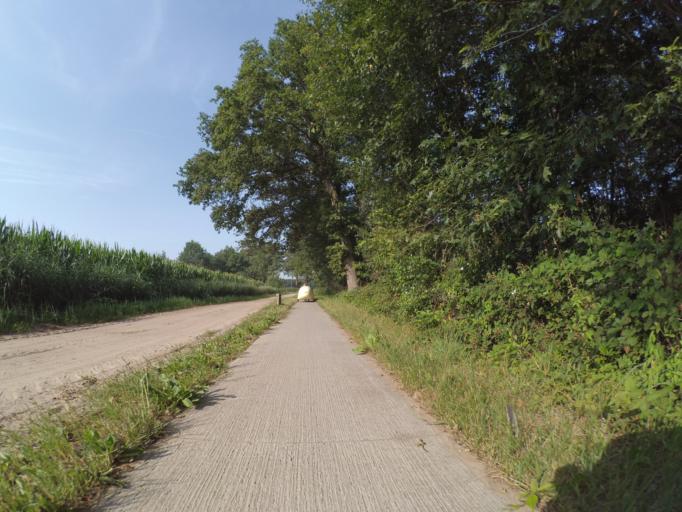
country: NL
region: Overijssel
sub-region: Gemeente Tubbergen
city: Tubbergen
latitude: 52.3595
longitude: 6.8459
